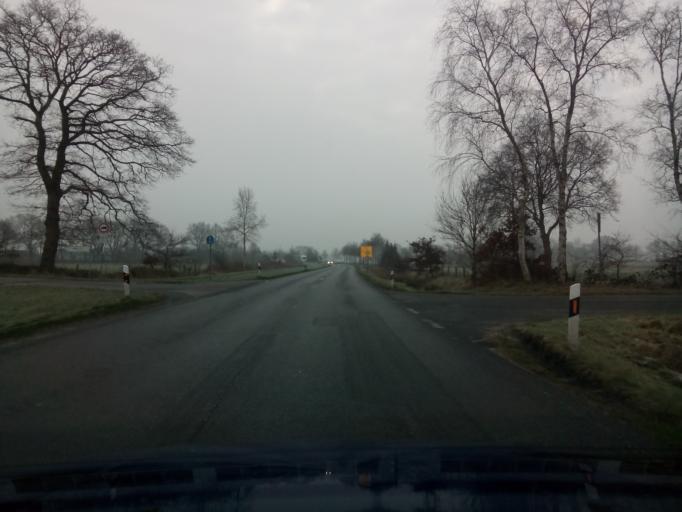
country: DE
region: Lower Saxony
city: Kuhrstedt
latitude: 53.6143
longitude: 8.8225
